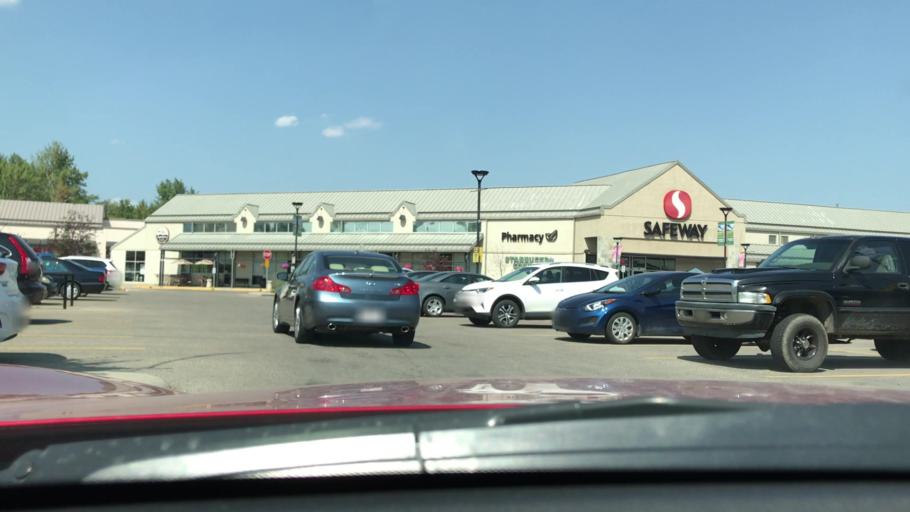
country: CA
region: Alberta
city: Calgary
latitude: 50.9733
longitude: -114.0978
